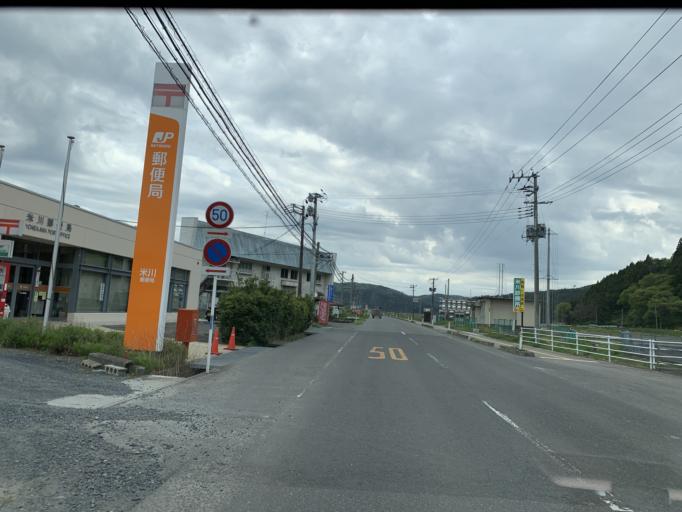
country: JP
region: Iwate
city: Ichinoseki
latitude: 38.7659
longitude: 141.3275
